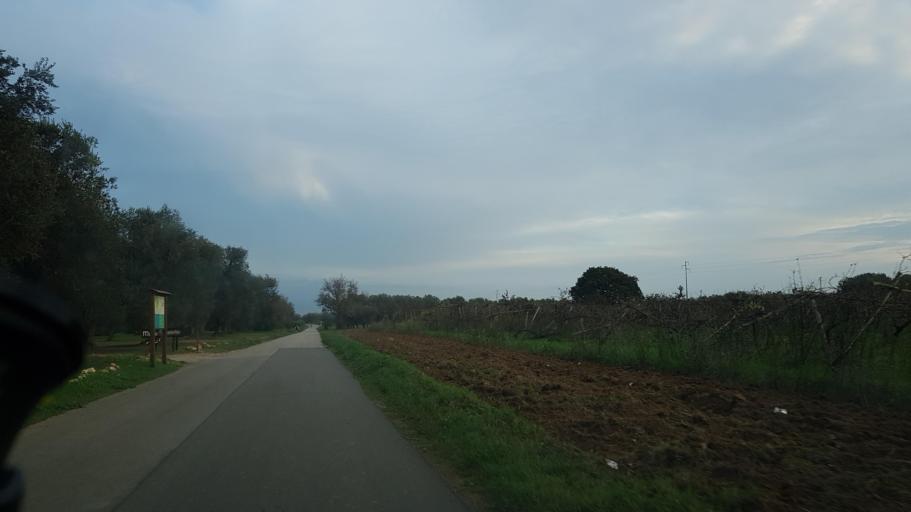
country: IT
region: Apulia
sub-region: Provincia di Brindisi
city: Latiano
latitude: 40.5420
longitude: 17.7376
